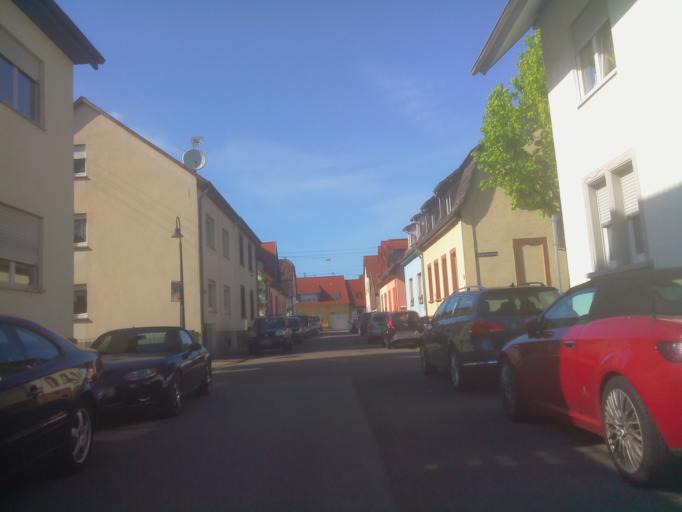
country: DE
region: Baden-Wuerttemberg
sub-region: Karlsruhe Region
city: Edingen-Neckarhausen
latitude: 49.4666
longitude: 8.5980
